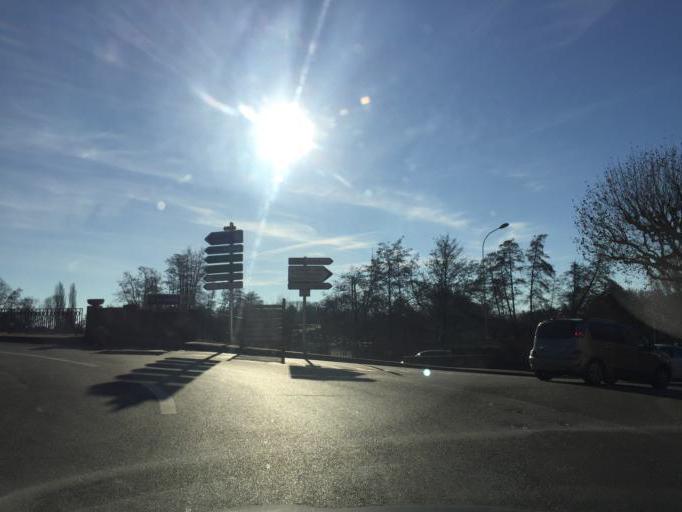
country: FR
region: Auvergne
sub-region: Departement de l'Allier
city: Saint-Pourcain-sur-Sioule
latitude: 46.3073
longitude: 3.2930
